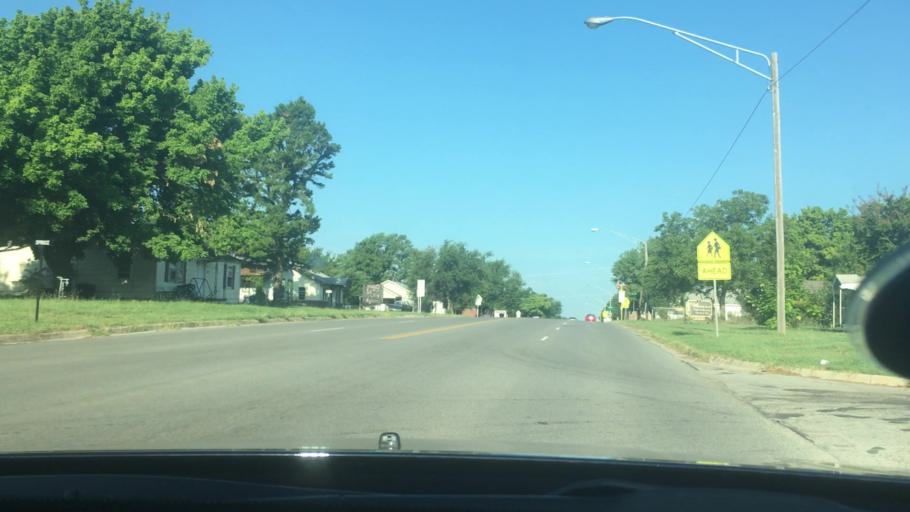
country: US
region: Oklahoma
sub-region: Garvin County
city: Stratford
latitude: 34.7967
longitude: -96.9576
